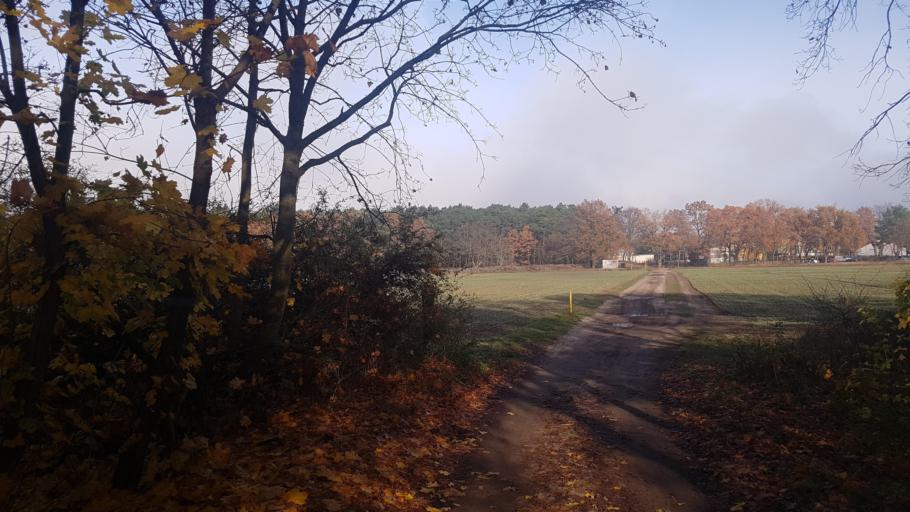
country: DE
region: Brandenburg
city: Golzow
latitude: 52.2822
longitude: 12.5974
